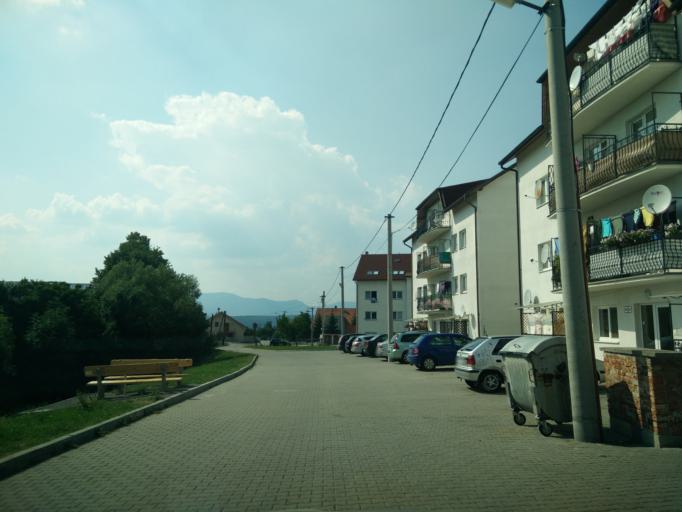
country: SK
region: Nitriansky
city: Prievidza
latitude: 48.7373
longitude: 18.6002
